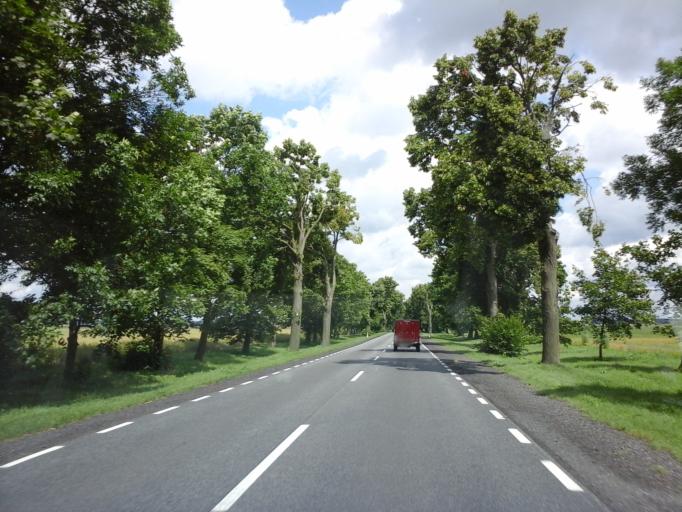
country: PL
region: Lubusz
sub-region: Powiat strzelecko-drezdenecki
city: Strzelce Krajenskie
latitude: 52.8924
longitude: 15.5700
